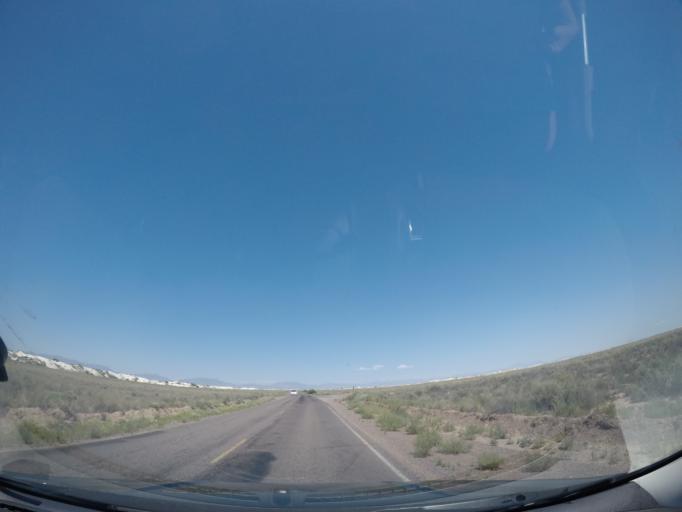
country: US
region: New Mexico
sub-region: Otero County
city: Holloman Air Force Base
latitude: 32.7918
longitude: -106.1978
